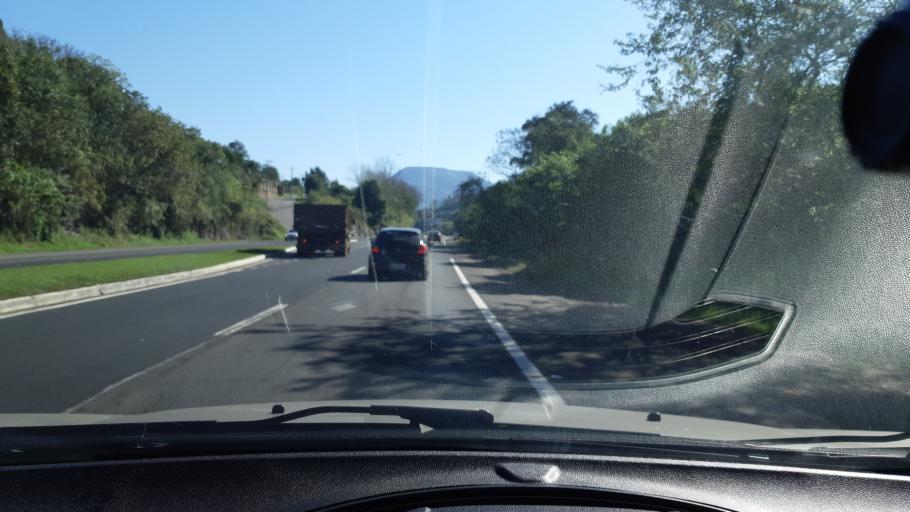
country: BR
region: Rio Grande do Sul
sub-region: Farroupilha
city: Farroupilha
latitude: -29.3903
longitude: -51.3604
